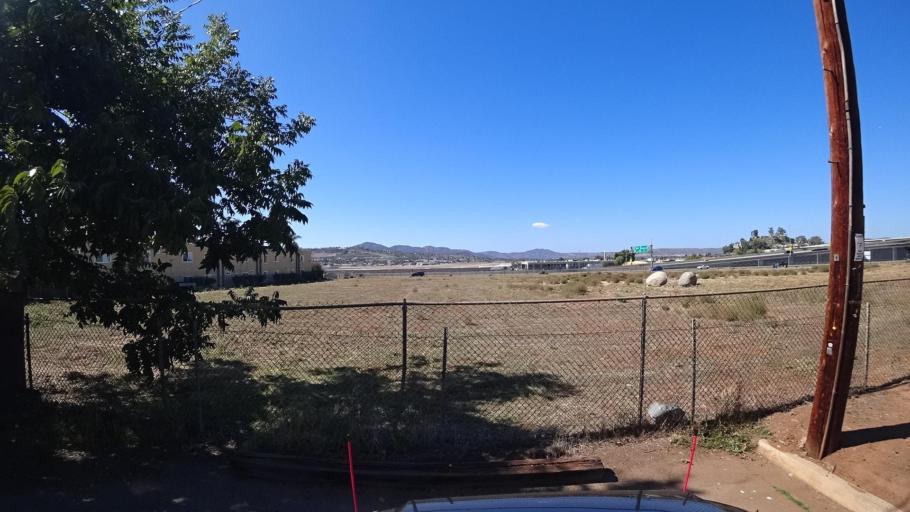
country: US
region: California
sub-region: San Diego County
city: Santee
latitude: 32.8273
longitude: -116.9603
